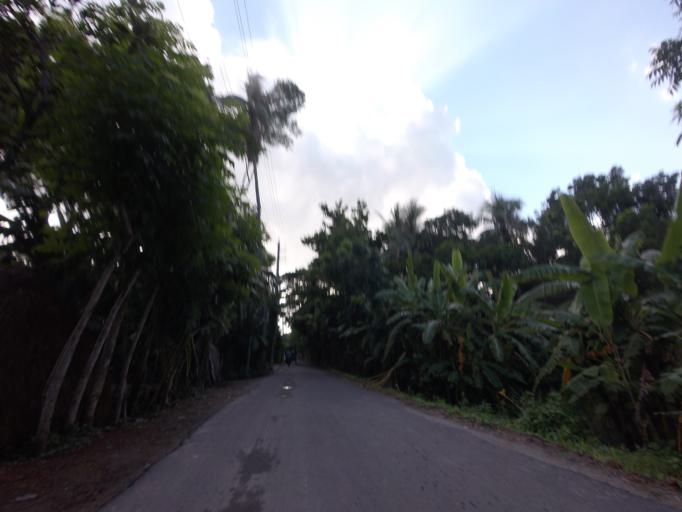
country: BD
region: Khulna
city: Kalia
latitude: 23.0367
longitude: 89.6280
